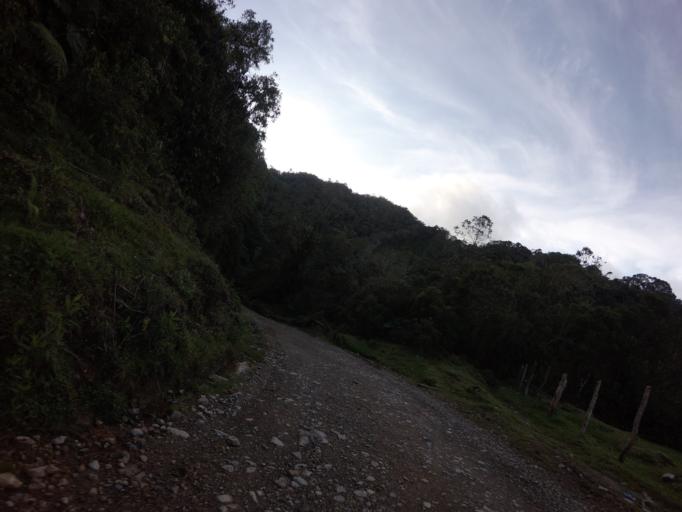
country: CO
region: Caldas
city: Pensilvania
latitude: 5.4343
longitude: -75.1312
